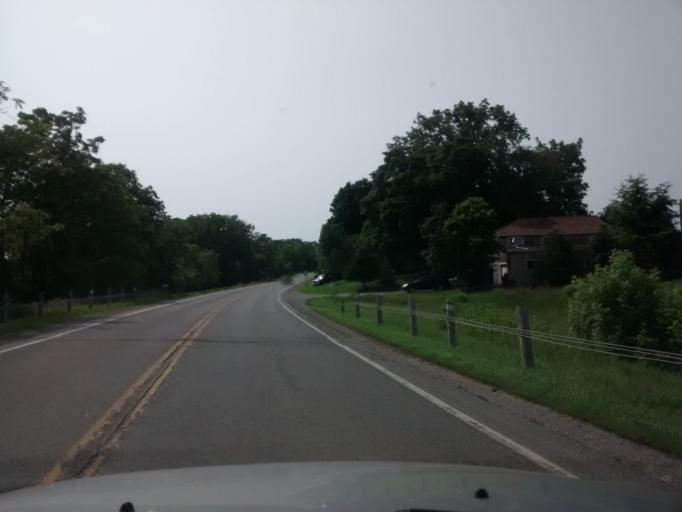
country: CA
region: Ontario
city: Ancaster
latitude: 43.0127
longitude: -79.8804
